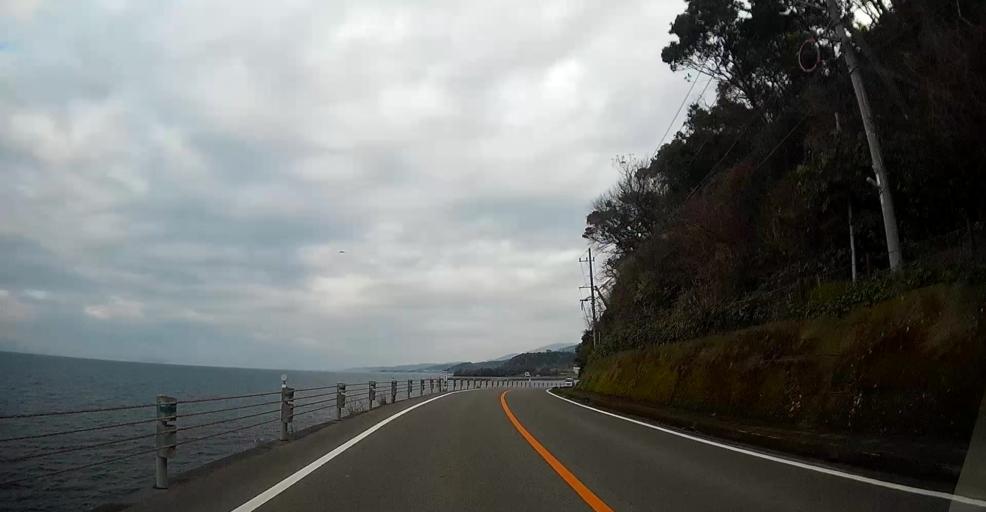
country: JP
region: Kumamoto
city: Hondo
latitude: 32.4572
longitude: 130.2167
